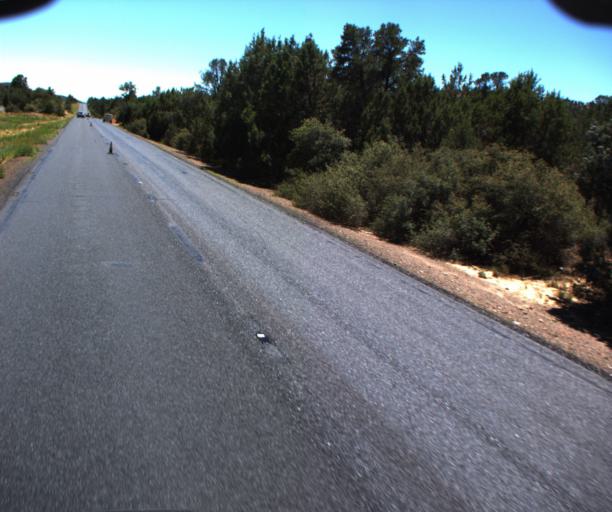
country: US
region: Arizona
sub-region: Gila County
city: Payson
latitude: 34.2130
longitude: -111.3320
